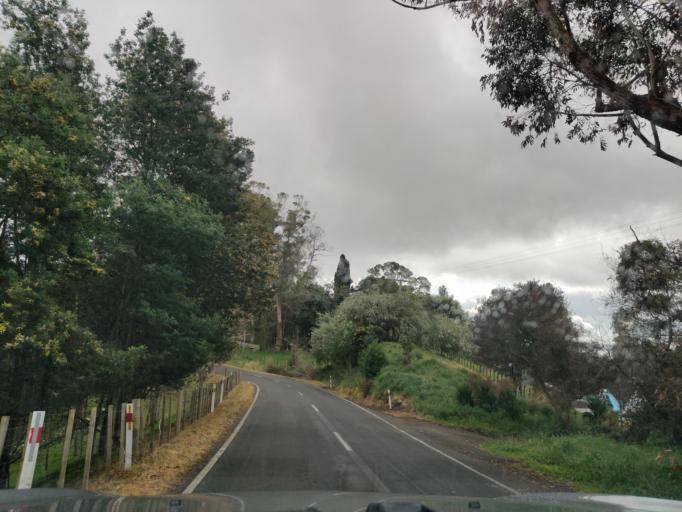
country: NZ
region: Hawke's Bay
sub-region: Hastings District
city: Hastings
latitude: -39.6793
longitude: 176.8964
